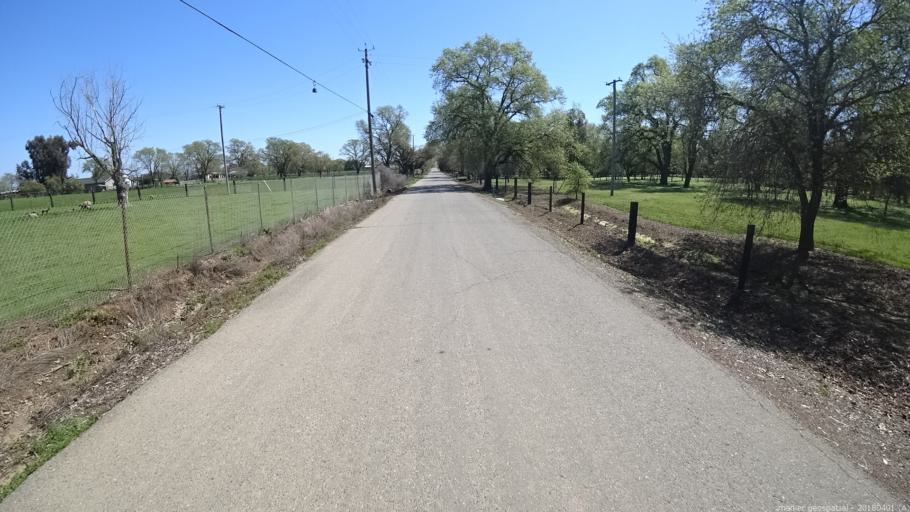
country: US
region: California
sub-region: Sacramento County
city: Rancho Murieta
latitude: 38.4492
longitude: -121.1683
